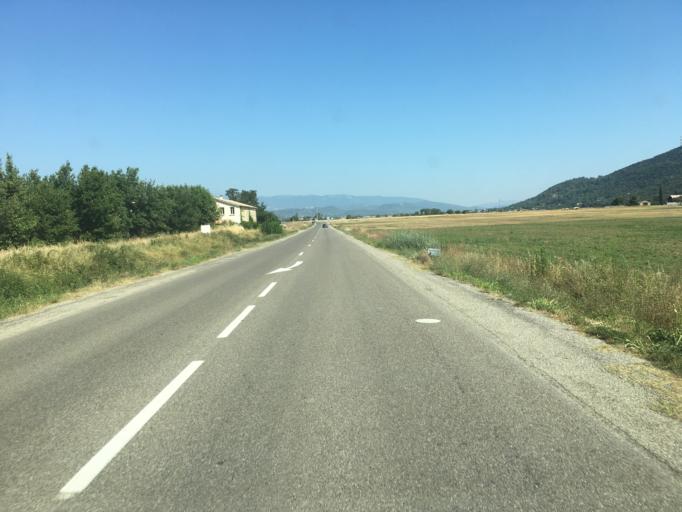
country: FR
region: Provence-Alpes-Cote d'Azur
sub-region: Departement des Alpes-de-Haute-Provence
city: Oraison
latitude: 43.8809
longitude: 5.9092
